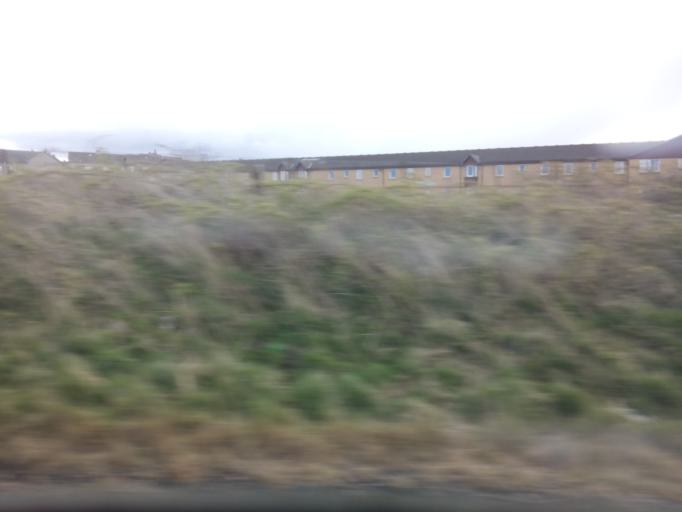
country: GB
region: Scotland
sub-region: East Lothian
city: Musselburgh
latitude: 55.9394
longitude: -3.0182
